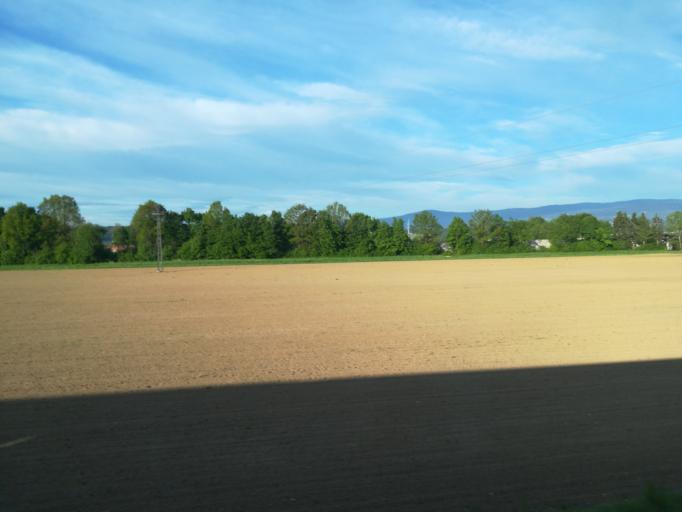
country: AT
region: Styria
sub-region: Politischer Bezirk Graz-Umgebung
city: Lieboch
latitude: 46.9755
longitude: 15.3257
